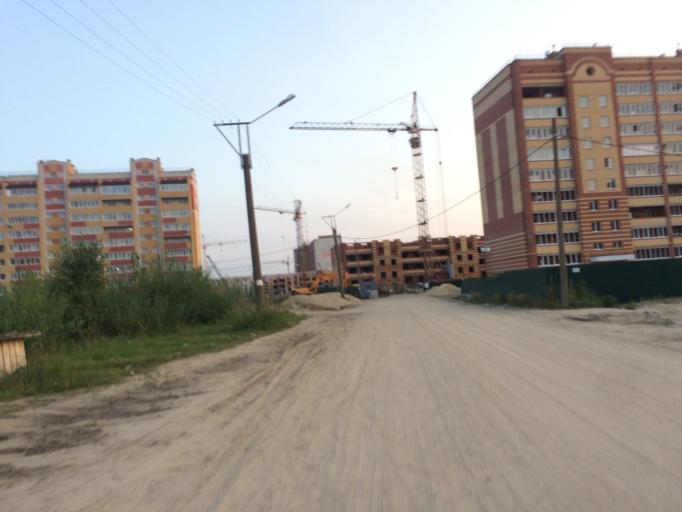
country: RU
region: Mariy-El
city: Yoshkar-Ola
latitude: 56.6419
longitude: 47.9209
